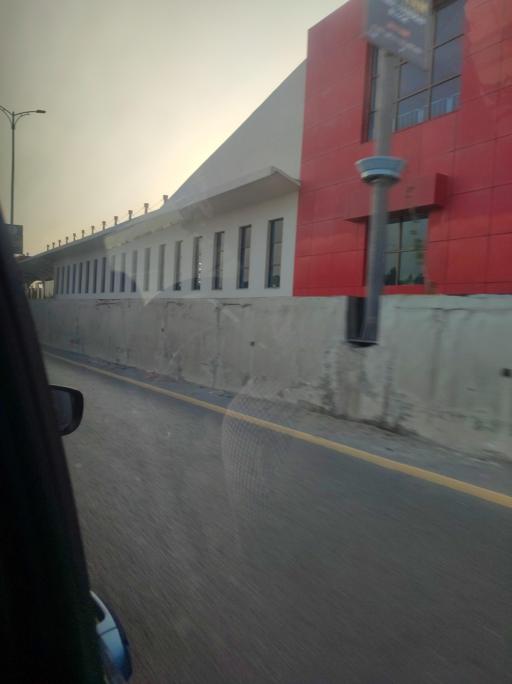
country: PK
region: Punjab
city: Rawalpindi
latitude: 33.6410
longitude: 72.9626
